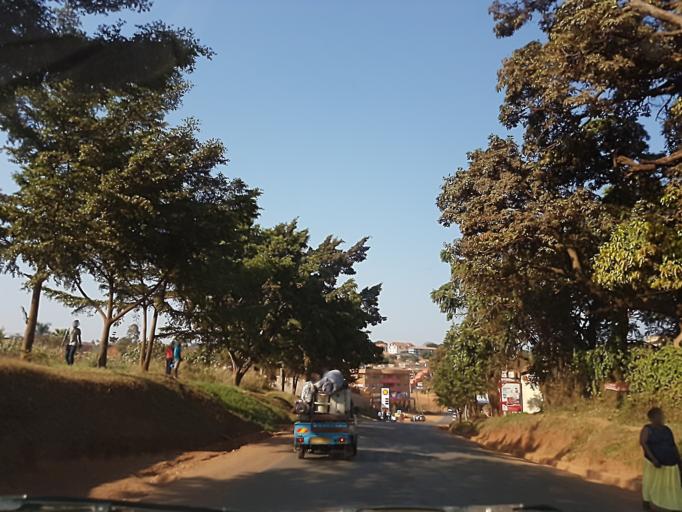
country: UG
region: Central Region
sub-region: Wakiso District
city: Kireka
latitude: 0.3405
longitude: 32.6153
